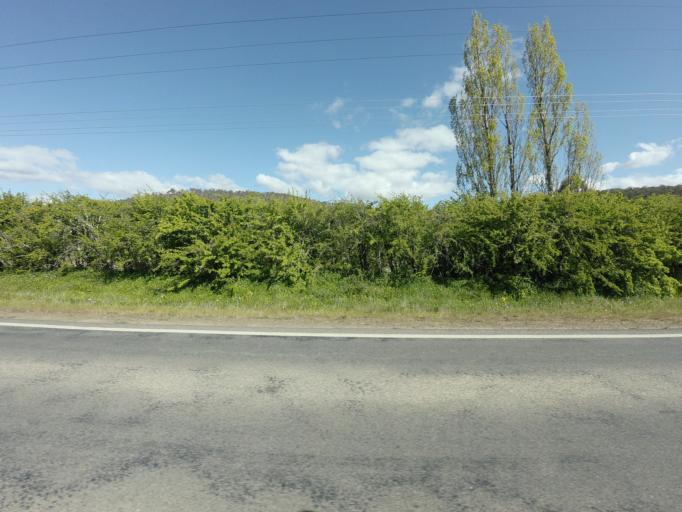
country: AU
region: Tasmania
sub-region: Derwent Valley
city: New Norfolk
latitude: -42.7782
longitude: 147.0459
